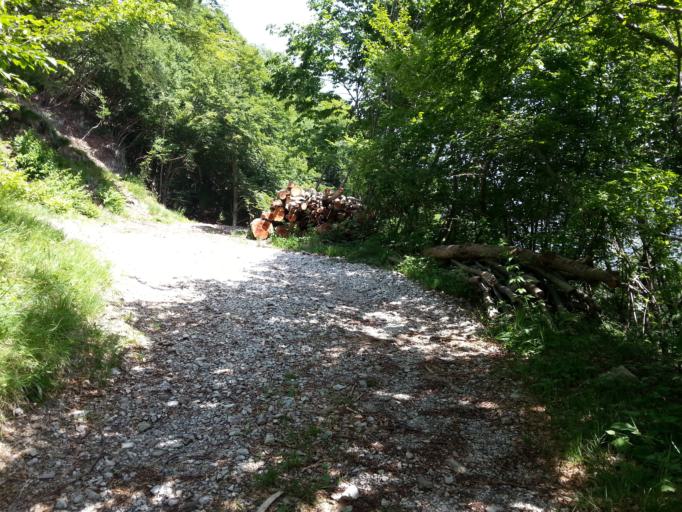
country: IT
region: Lombardy
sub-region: Provincia di Lecco
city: Cremeno
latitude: 45.9139
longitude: 9.4560
